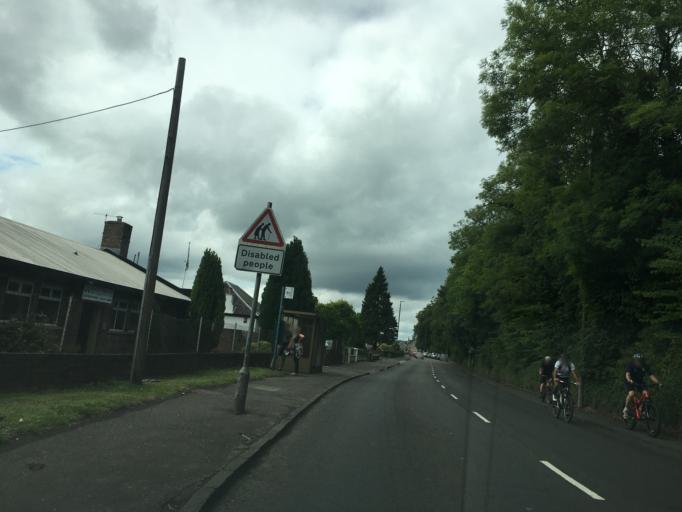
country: GB
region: Scotland
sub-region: Stirling
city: Stirling
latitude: 56.1361
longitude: -3.9181
